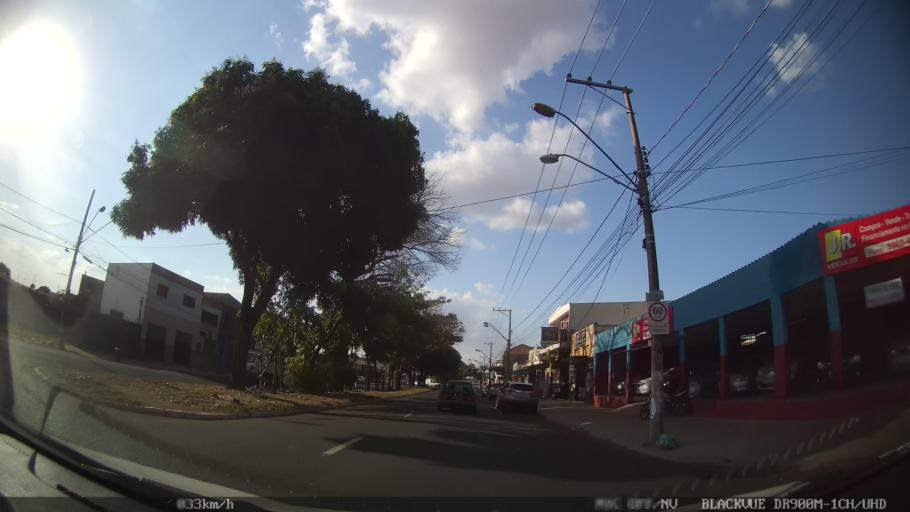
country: BR
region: Sao Paulo
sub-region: Ribeirao Preto
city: Ribeirao Preto
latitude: -21.1521
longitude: -47.8048
